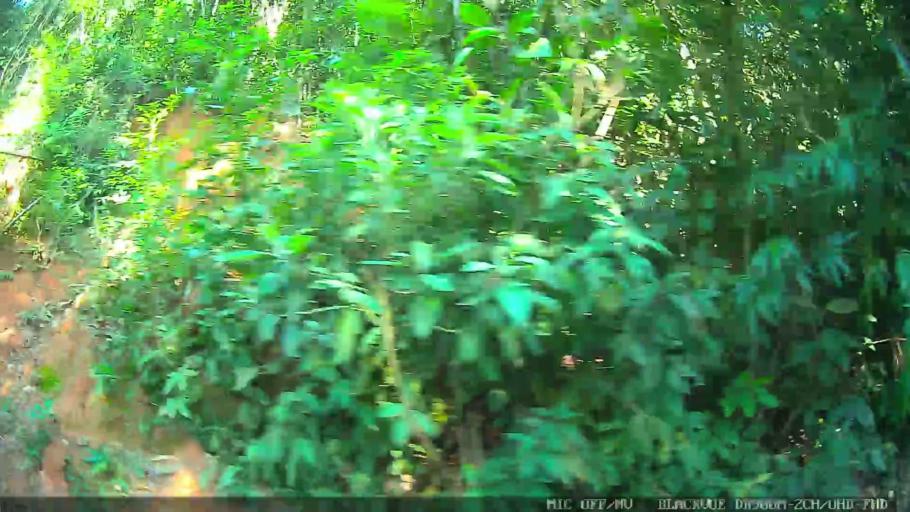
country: BR
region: Sao Paulo
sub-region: Guaruja
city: Guaruja
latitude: -23.9823
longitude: -46.2585
